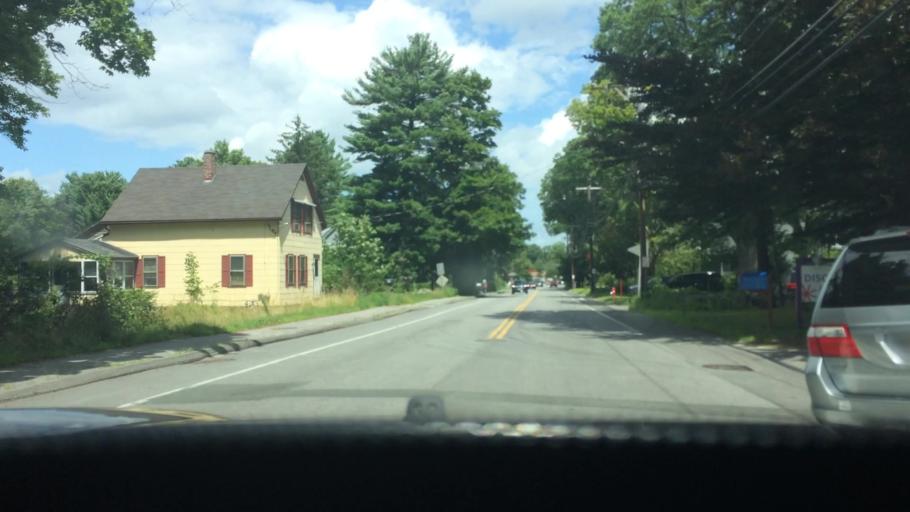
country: US
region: Massachusetts
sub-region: Middlesex County
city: Acton
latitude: 42.4648
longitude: -71.4565
